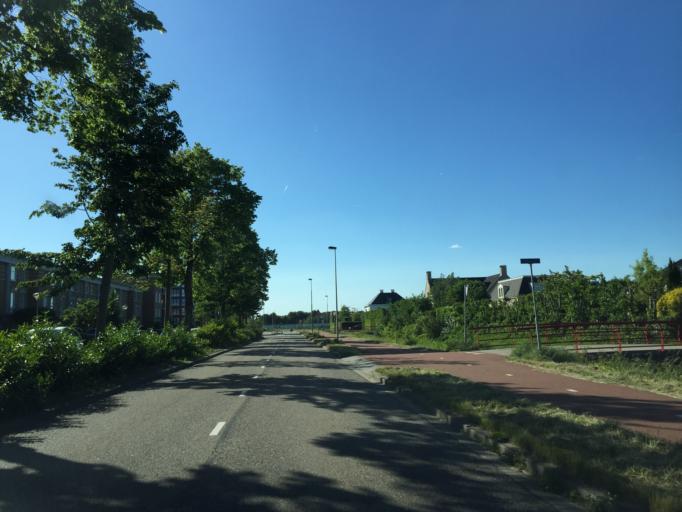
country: NL
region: South Holland
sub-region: Gemeente Lansingerland
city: Bergschenhoek
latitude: 51.9990
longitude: 4.5029
